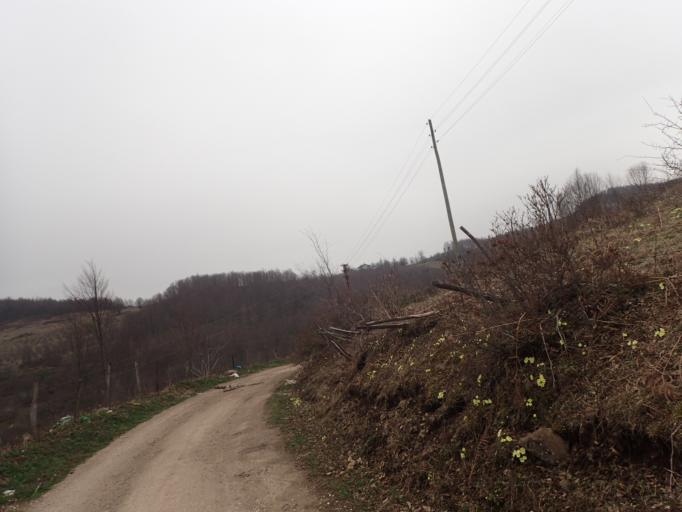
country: TR
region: Ordu
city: Kumru
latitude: 40.7858
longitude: 37.1953
